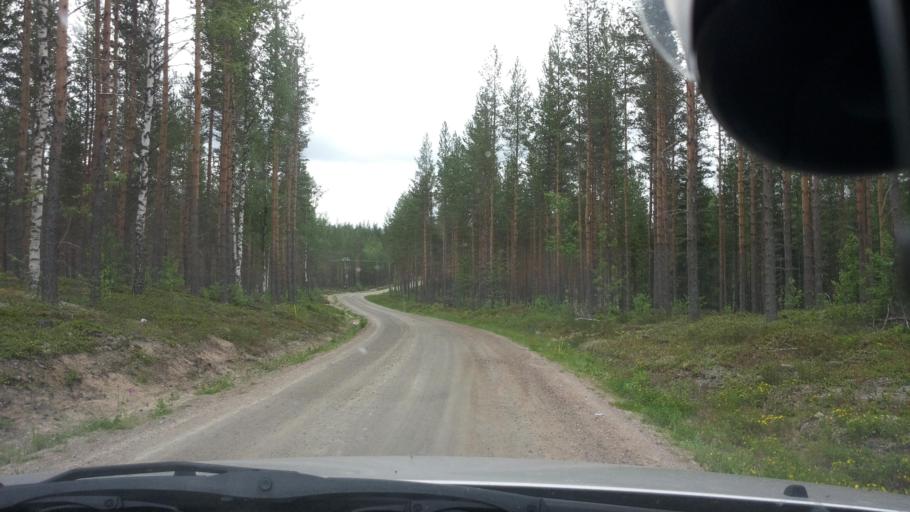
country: SE
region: Gaevleborg
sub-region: Ovanakers Kommun
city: Edsbyn
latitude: 61.5225
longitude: 15.3559
